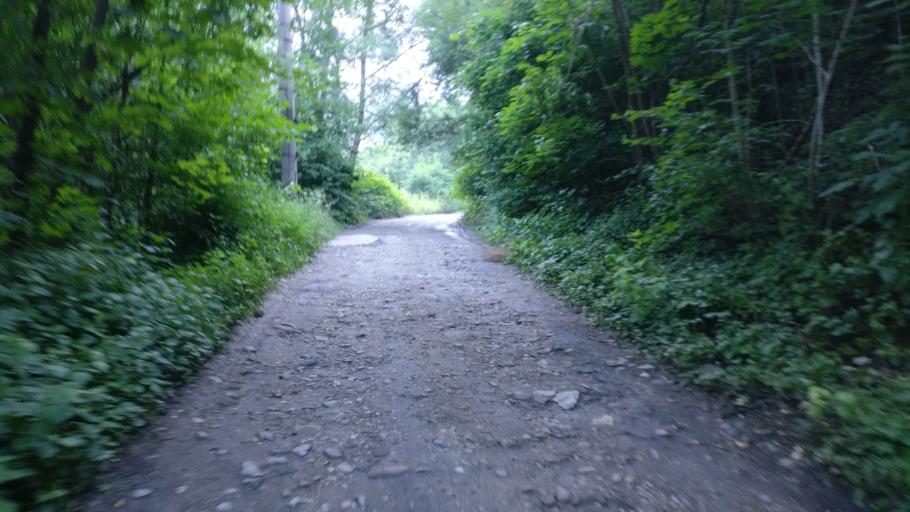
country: SK
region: Zilinsky
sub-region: Okres Zilina
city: Zilina
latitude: 49.2436
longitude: 18.7452
